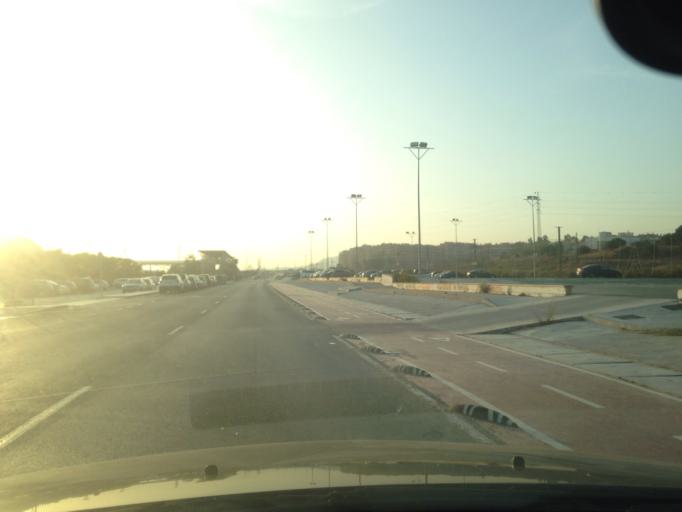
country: ES
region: Andalusia
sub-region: Provincia de Malaga
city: Malaga
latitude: 36.7161
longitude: -4.4786
